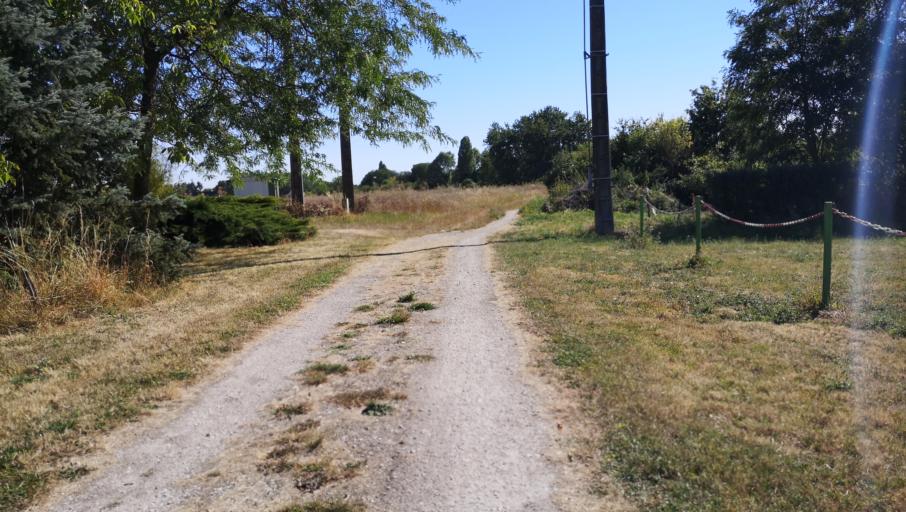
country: FR
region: Centre
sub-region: Departement du Loiret
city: Semoy
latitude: 47.9338
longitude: 1.9596
